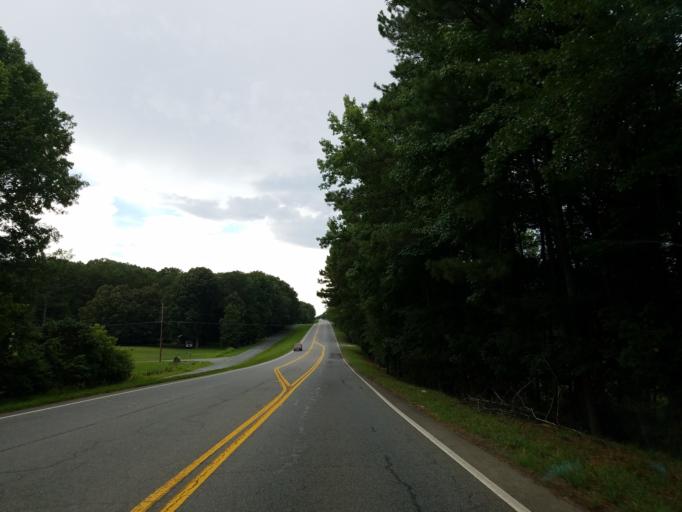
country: US
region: Georgia
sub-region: Bartow County
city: Adairsville
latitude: 34.2912
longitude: -84.8746
